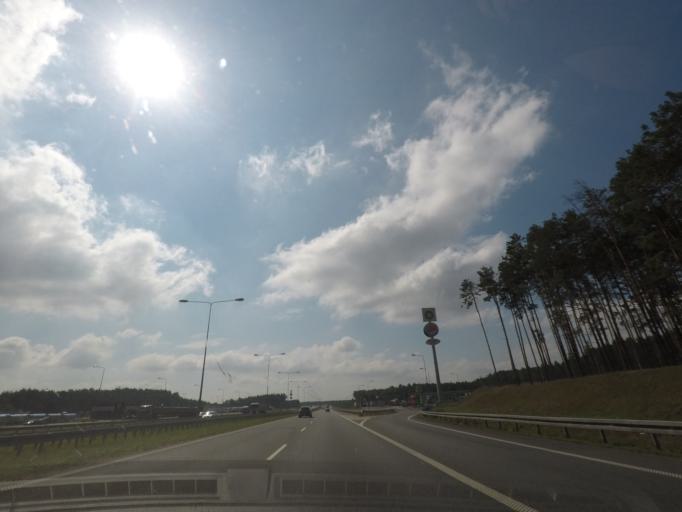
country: PL
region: Kujawsko-Pomorskie
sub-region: Powiat aleksandrowski
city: Aleksandrow Kujawski
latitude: 52.9034
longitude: 18.7214
